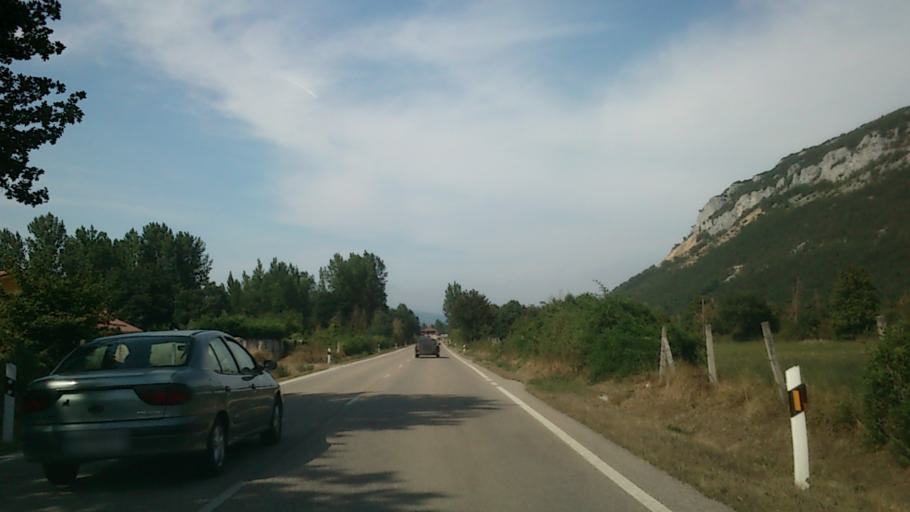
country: ES
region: Castille and Leon
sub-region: Provincia de Burgos
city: Espinosa de los Monteros
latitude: 43.0309
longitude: -3.4834
